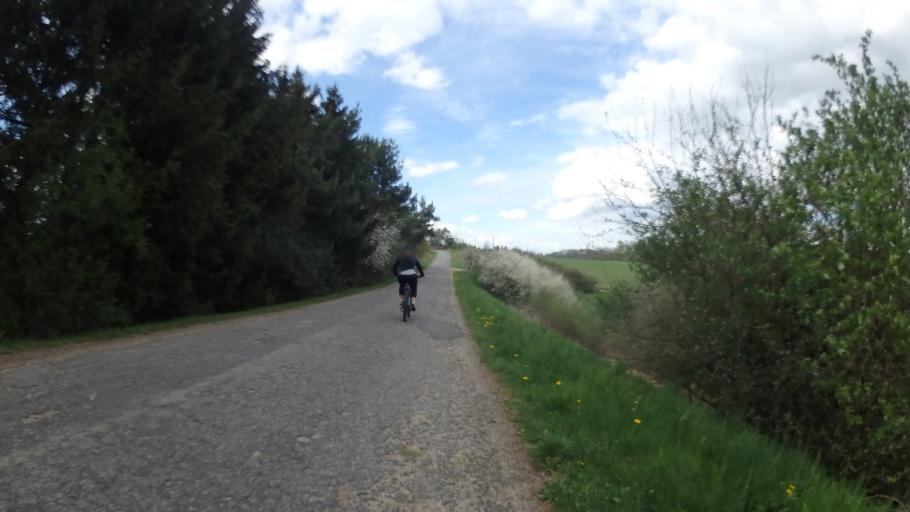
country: CZ
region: Vysocina
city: Merin
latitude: 49.3540
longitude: 15.9354
